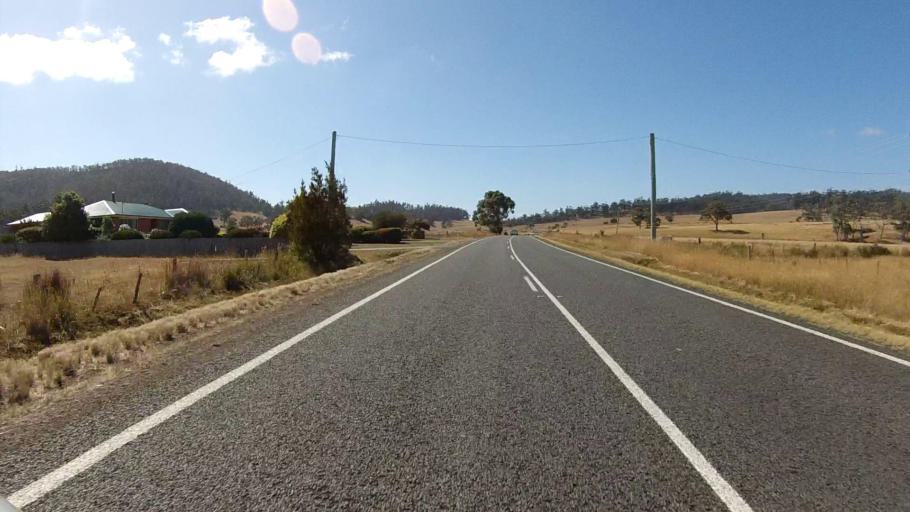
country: AU
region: Tasmania
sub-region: Sorell
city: Sorell
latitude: -42.4407
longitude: 147.9280
